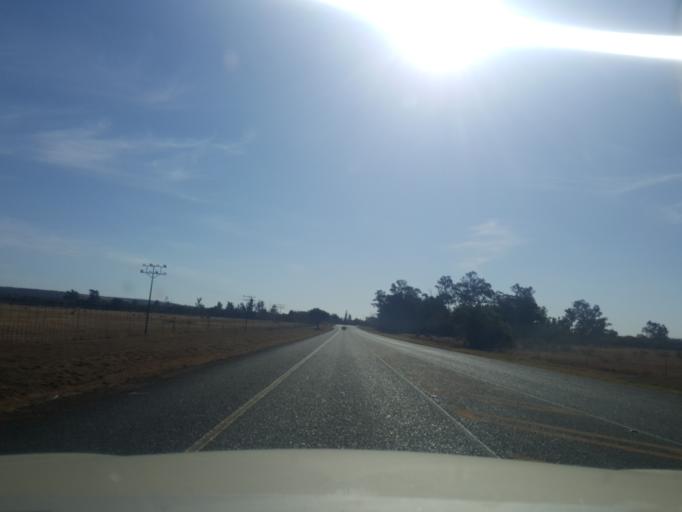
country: ZA
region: North-West
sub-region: Ngaka Modiri Molema District Municipality
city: Zeerust
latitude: -25.5607
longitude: 26.2233
